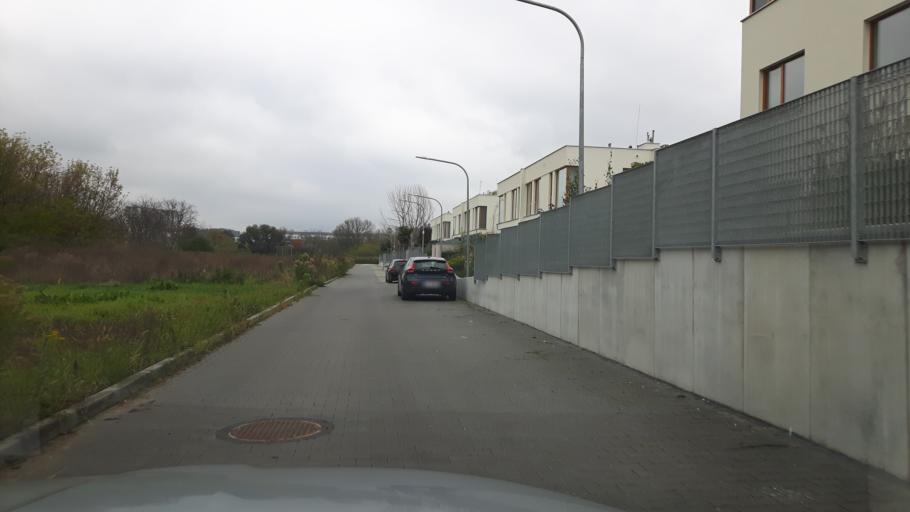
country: PL
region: Masovian Voivodeship
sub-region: Warszawa
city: Mokotow
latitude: 52.1791
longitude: 21.0347
